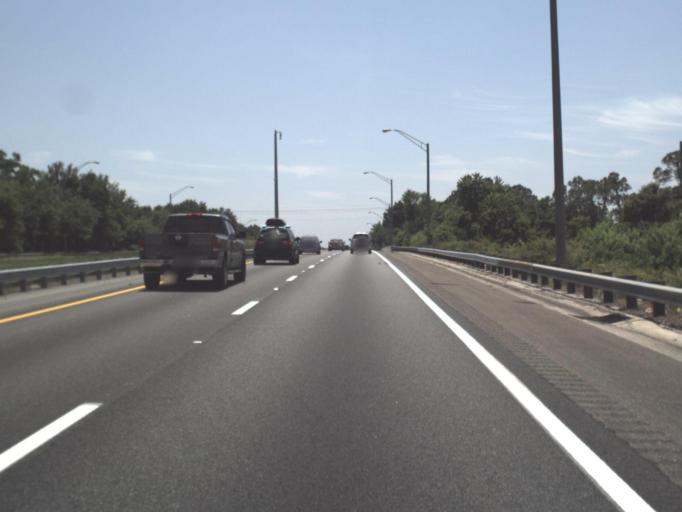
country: US
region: Florida
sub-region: Duval County
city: Jacksonville
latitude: 30.3962
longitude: -81.7567
